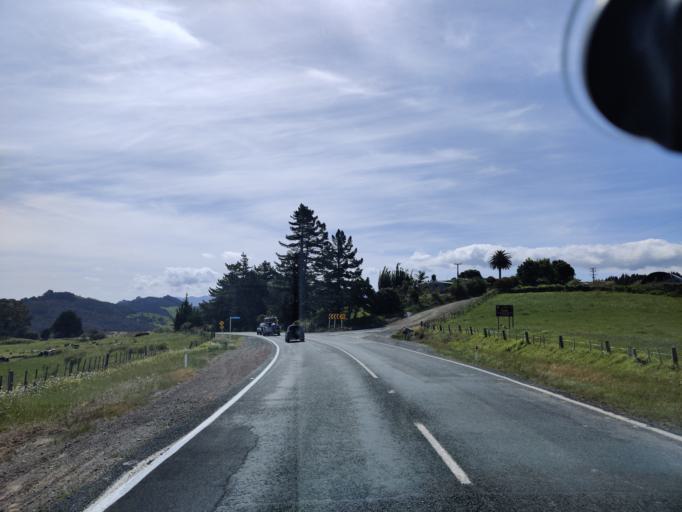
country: NZ
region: Northland
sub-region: Far North District
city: Kaitaia
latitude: -35.4570
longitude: 173.4760
